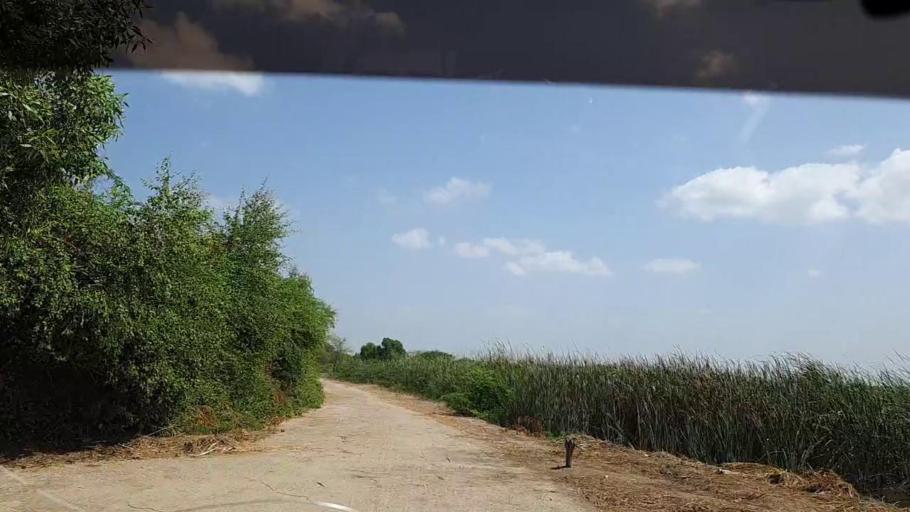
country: PK
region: Sindh
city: Badin
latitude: 24.5898
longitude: 68.8029
